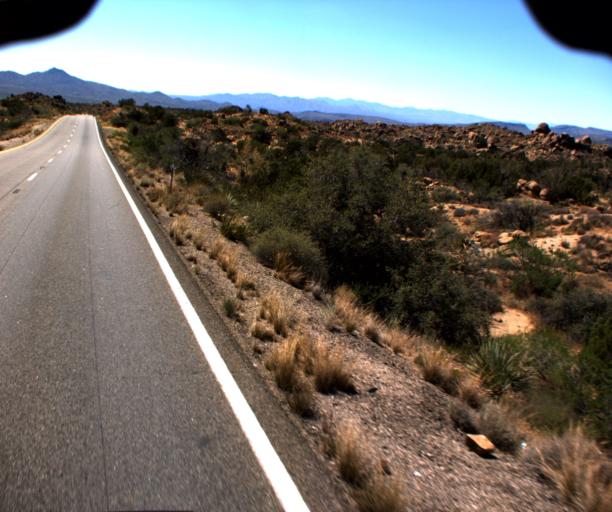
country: US
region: Arizona
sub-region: Yavapai County
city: Bagdad
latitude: 34.4836
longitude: -113.3540
